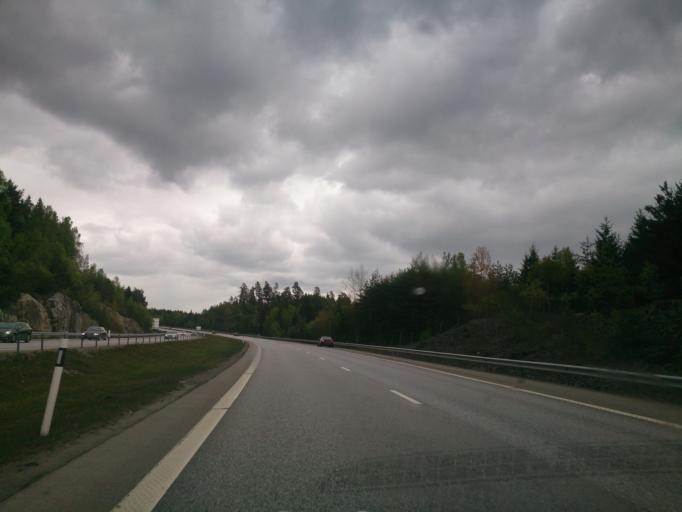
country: SE
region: Soedermanland
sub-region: Trosa Kommun
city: Vagnharad
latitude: 58.9740
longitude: 17.5232
